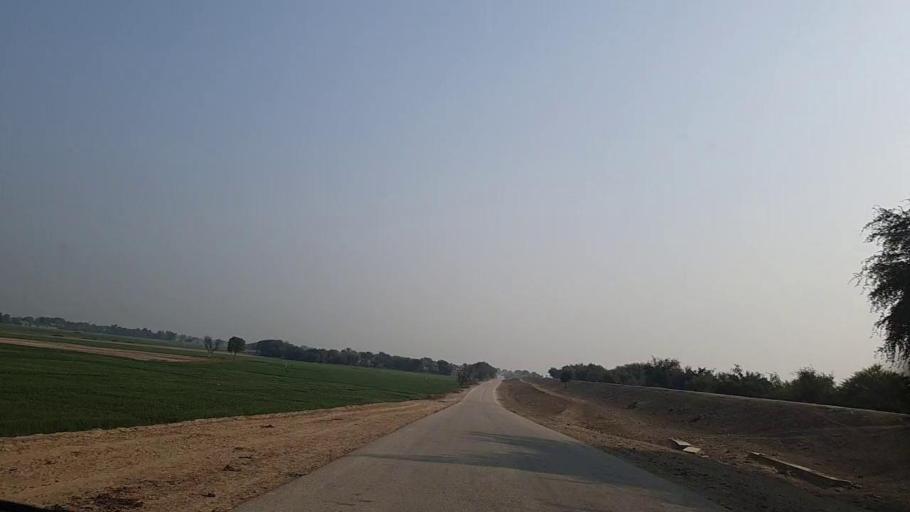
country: PK
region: Sindh
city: Sann
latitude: 26.1676
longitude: 68.1097
